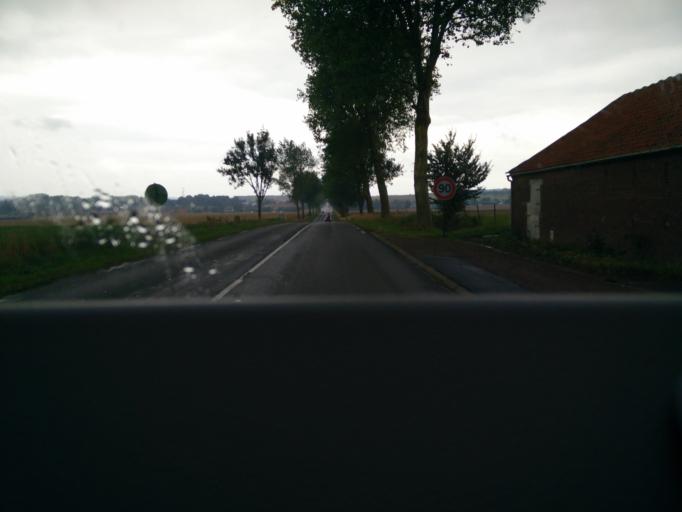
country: FR
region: Nord-Pas-de-Calais
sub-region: Departement du Pas-de-Calais
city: Savy-Berlette
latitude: 50.3481
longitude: 2.5689
